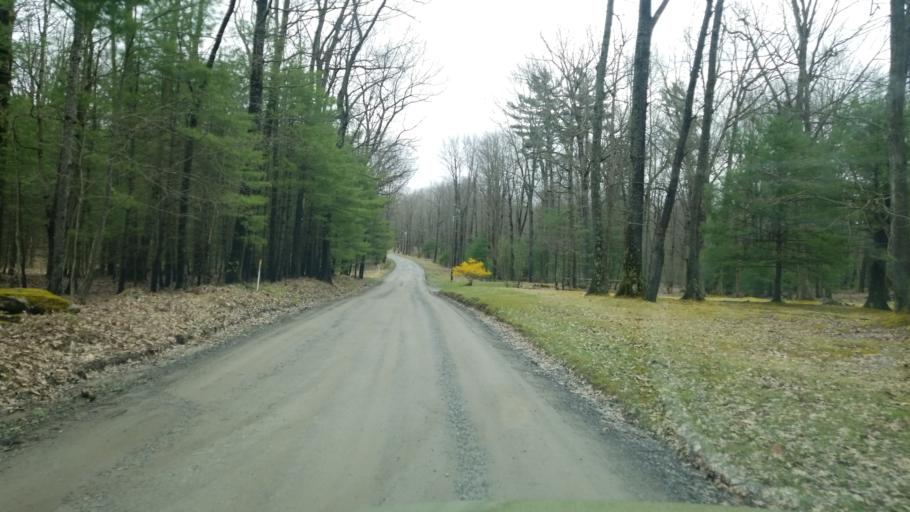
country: US
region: Pennsylvania
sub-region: Clearfield County
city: Shiloh
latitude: 41.1789
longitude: -78.3293
